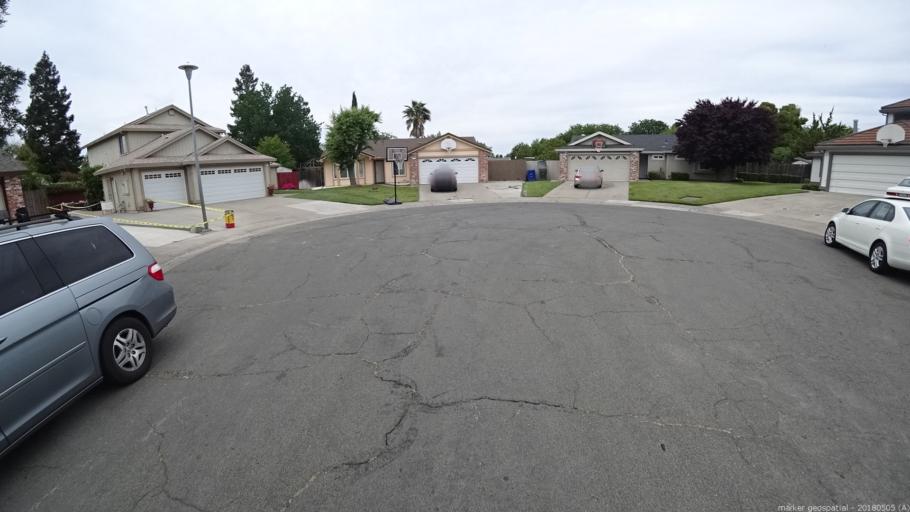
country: US
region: California
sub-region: Sacramento County
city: Rio Linda
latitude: 38.6526
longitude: -121.4634
